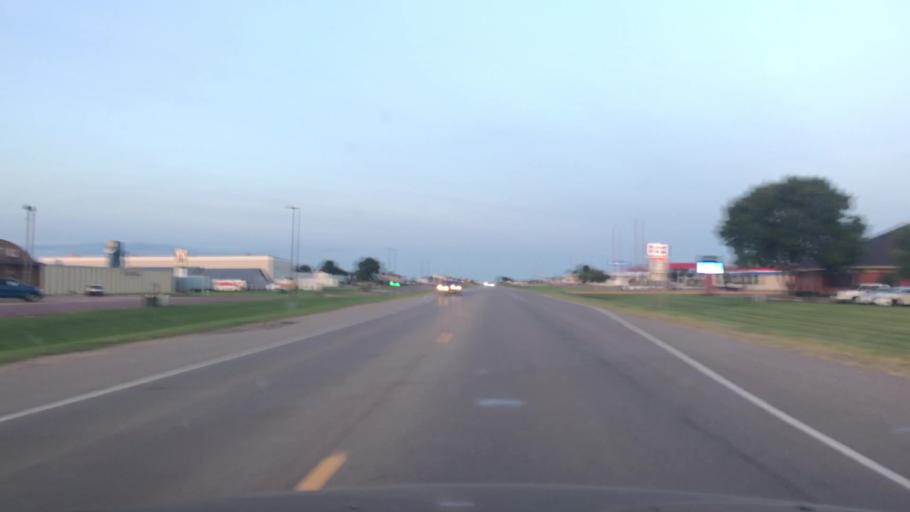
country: US
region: Minnesota
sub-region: Redwood County
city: Redwood Falls
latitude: 44.5414
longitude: -95.0921
